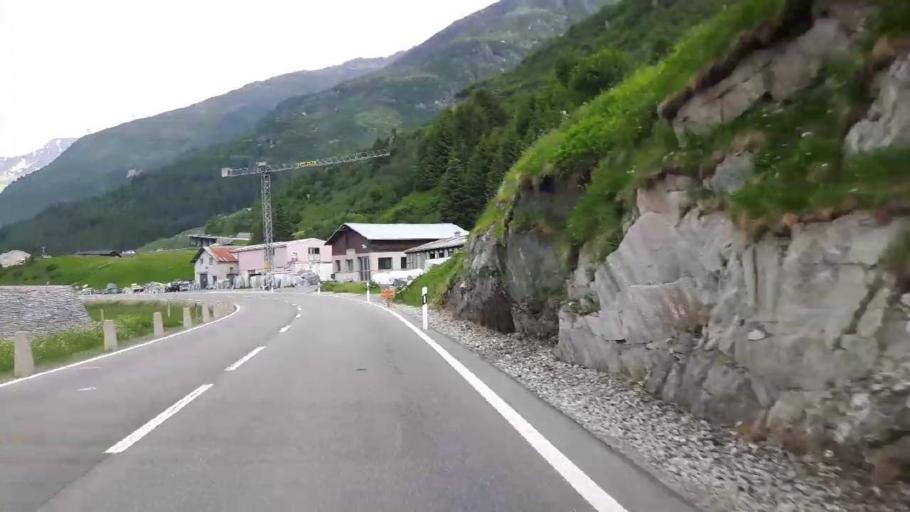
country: CH
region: Uri
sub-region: Uri
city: Andermatt
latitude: 46.6160
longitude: 8.5592
